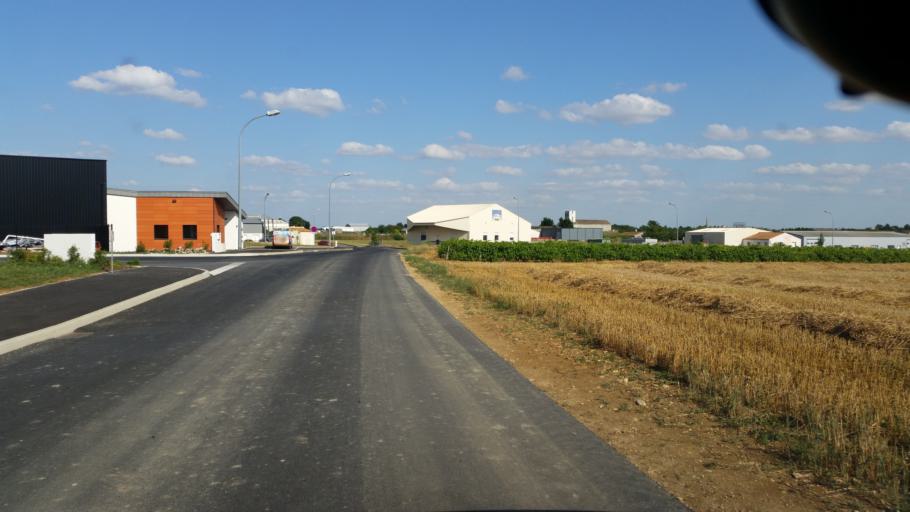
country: FR
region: Poitou-Charentes
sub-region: Departement de la Charente-Maritime
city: Saint-Jean-de-Liversay
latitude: 46.2327
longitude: -0.8859
